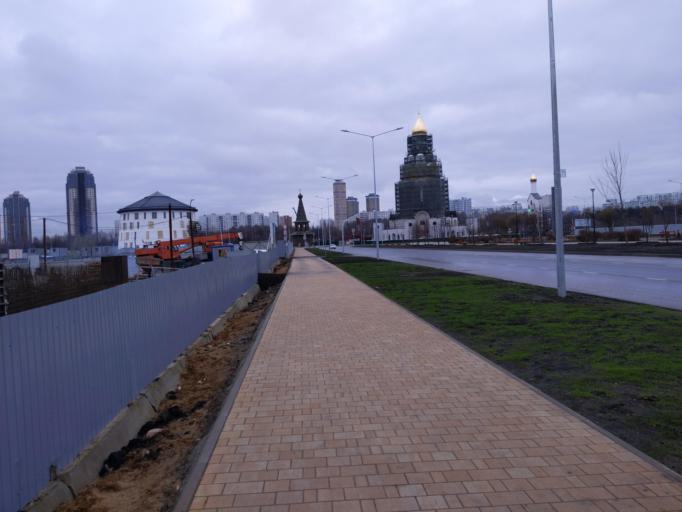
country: RU
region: Moscow
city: Strogino
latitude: 55.8147
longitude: 37.4241
